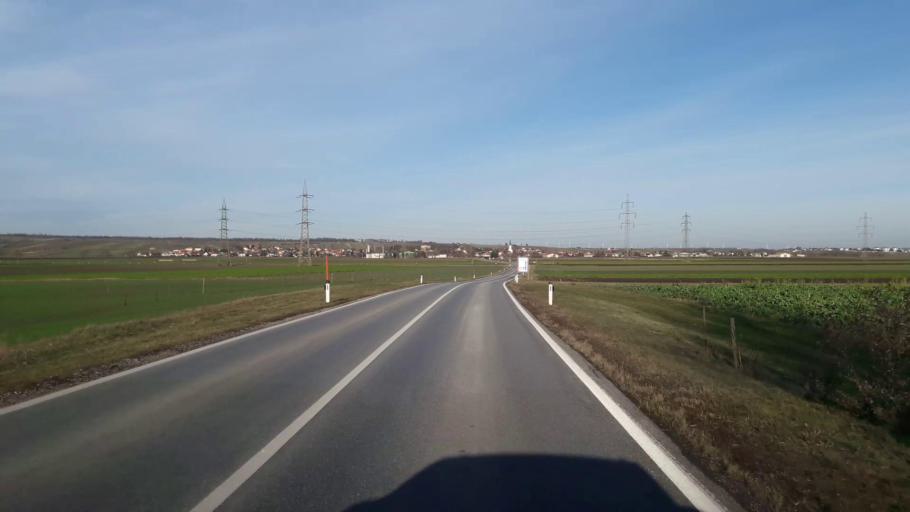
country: AT
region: Lower Austria
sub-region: Politischer Bezirk Mistelbach
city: Bockfliess
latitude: 48.3433
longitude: 16.5955
